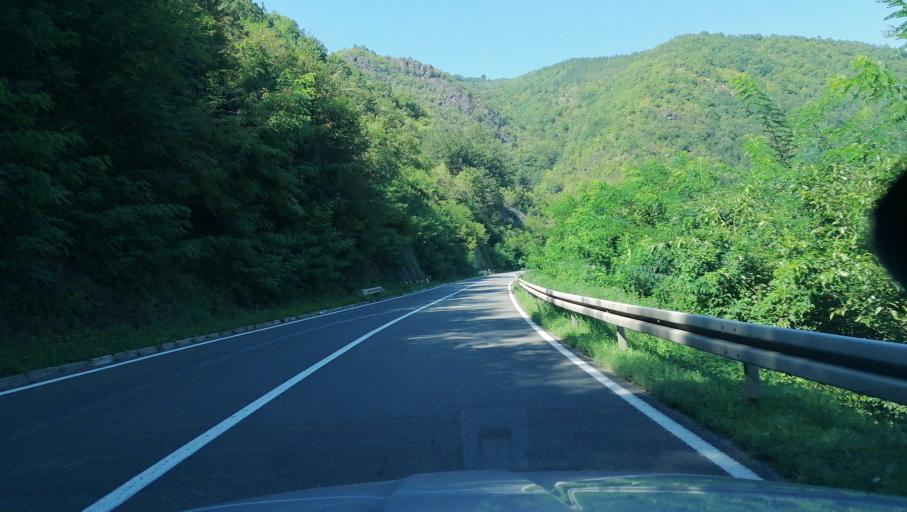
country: RS
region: Central Serbia
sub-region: Raski Okrug
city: Kraljevo
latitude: 43.6300
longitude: 20.5427
